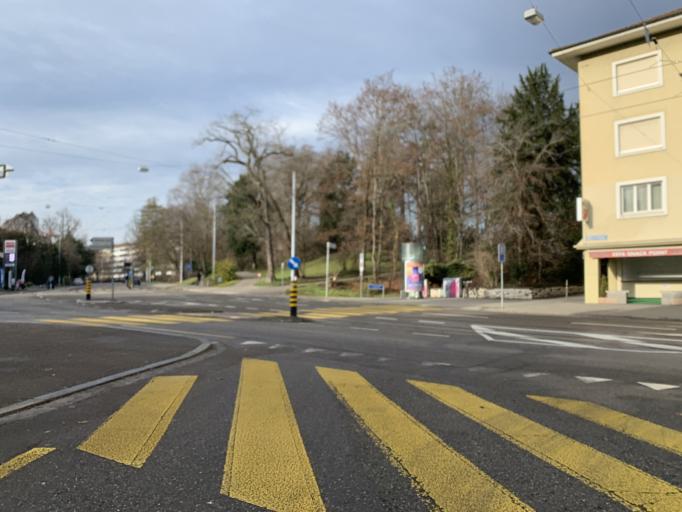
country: CH
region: Basel-Landschaft
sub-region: Bezirk Arlesheim
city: Birsfelden
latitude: 47.5527
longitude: 7.6057
